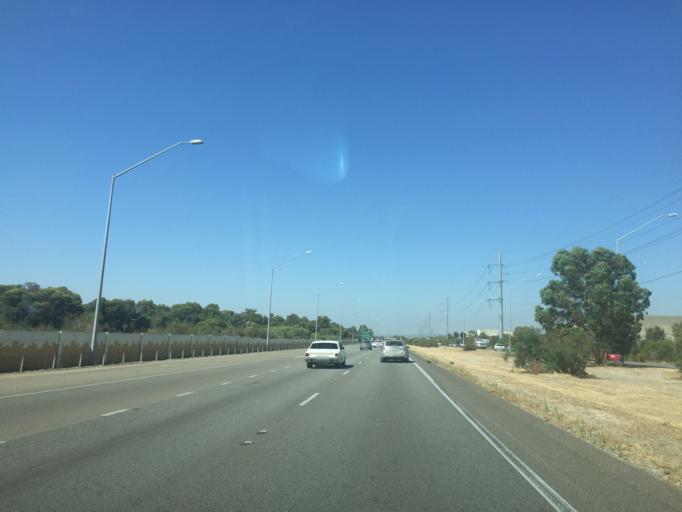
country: AU
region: Western Australia
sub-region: Canning
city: Willetton
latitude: -32.0651
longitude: 115.8945
